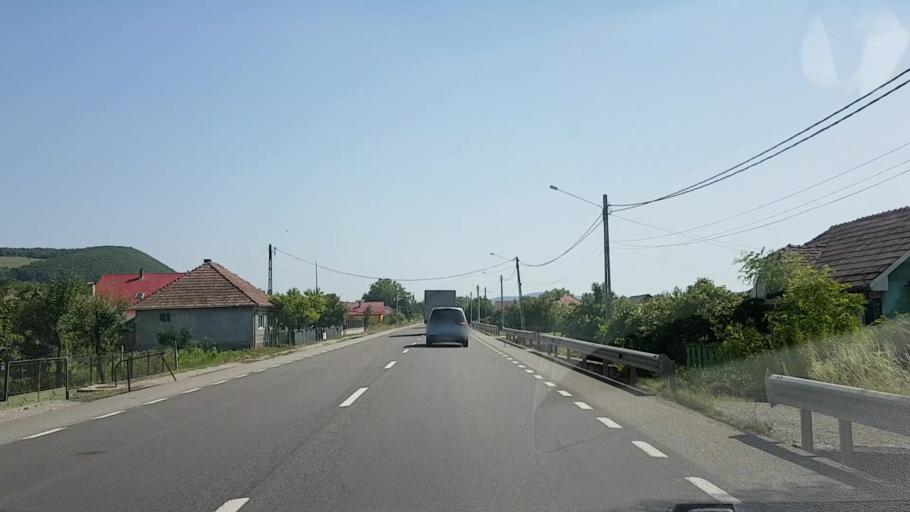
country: RO
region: Bistrita-Nasaud
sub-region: Comuna Sieu-Odorhei
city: Sieu-Odorhei
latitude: 47.1547
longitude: 24.3061
